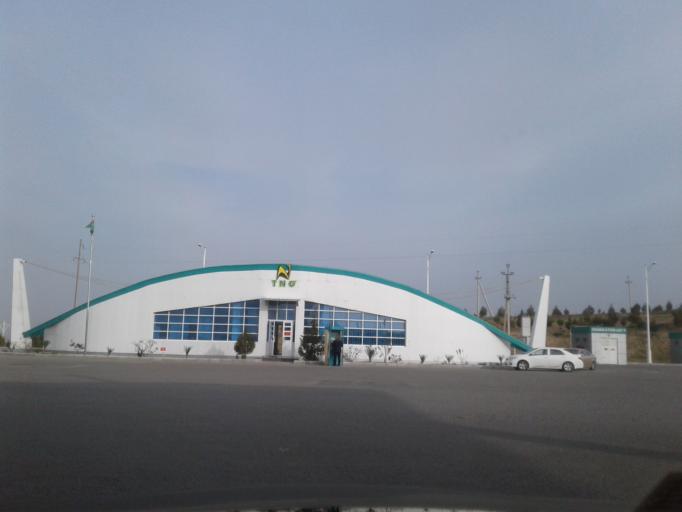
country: TM
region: Ahal
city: Annau
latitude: 37.8769
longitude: 58.4301
